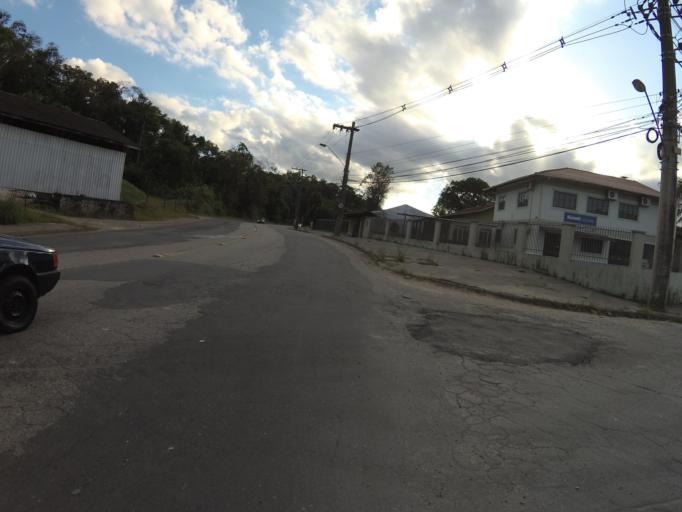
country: BR
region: Santa Catarina
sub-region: Blumenau
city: Blumenau
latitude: -26.8821
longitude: -49.1051
